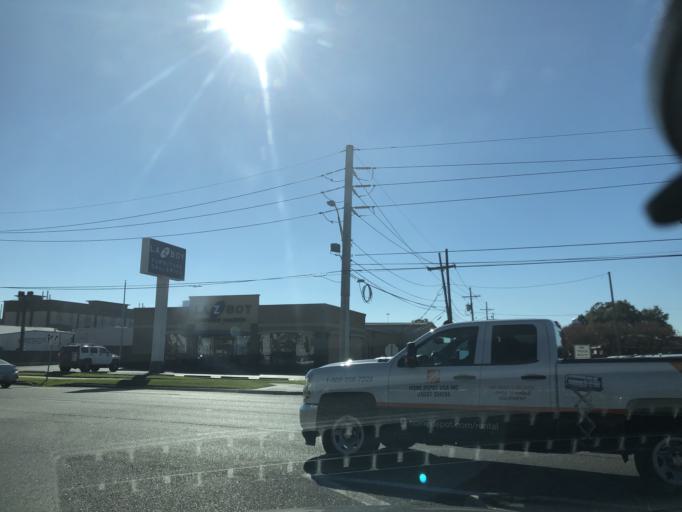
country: US
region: Louisiana
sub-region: Jefferson Parish
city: Metairie
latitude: 30.0032
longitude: -90.1573
